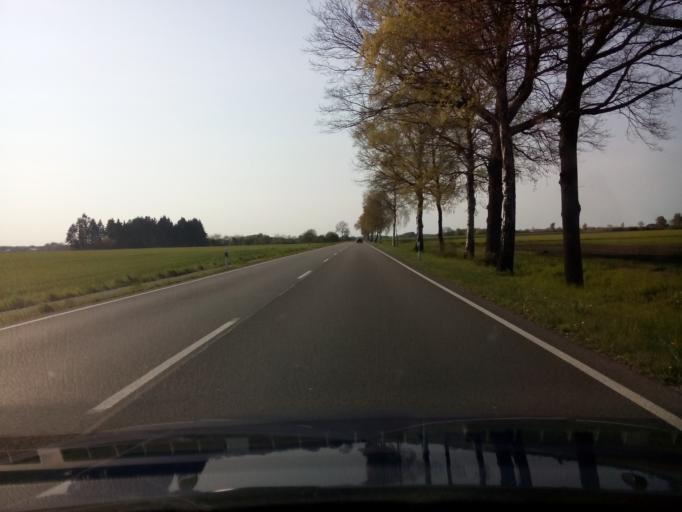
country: DE
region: Lower Saxony
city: Engeln
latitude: 52.8226
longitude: 8.9406
